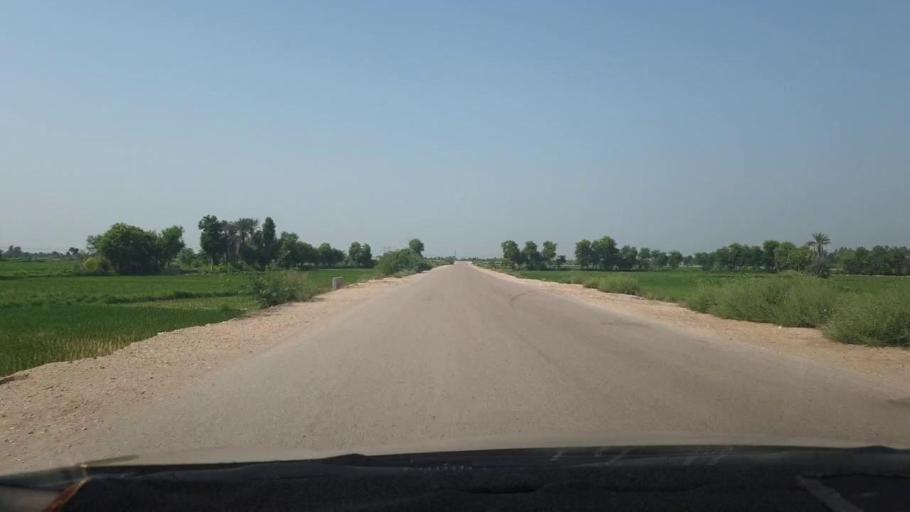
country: PK
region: Sindh
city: Larkana
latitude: 27.5991
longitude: 68.2432
